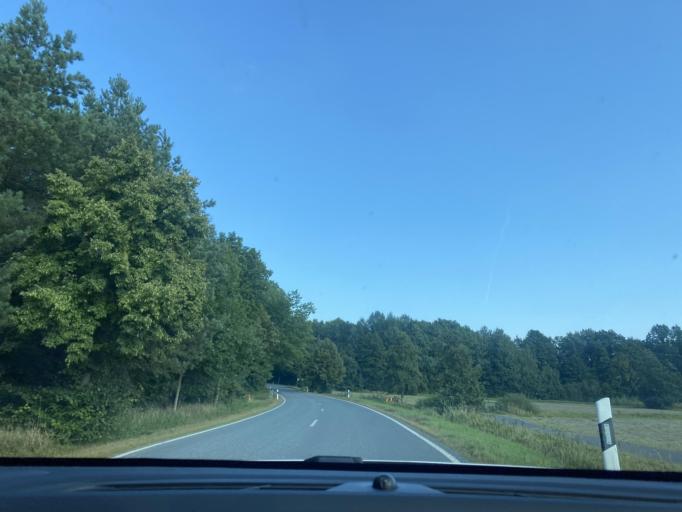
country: DE
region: Saxony
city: Quitzdorf
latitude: 51.2465
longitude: 14.7822
